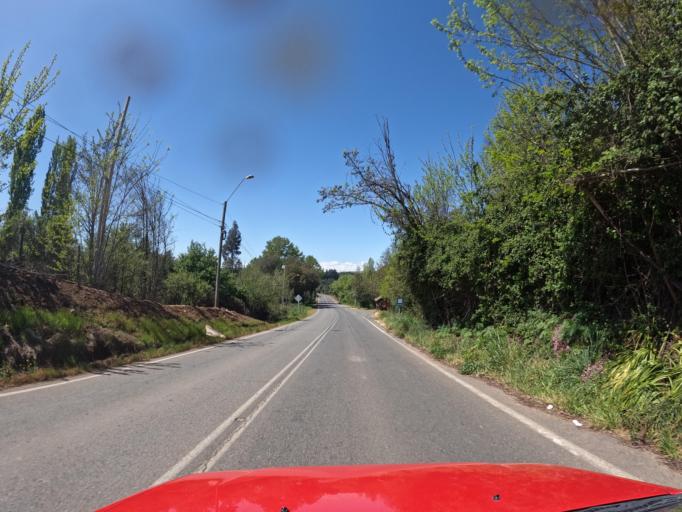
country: CL
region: Maule
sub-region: Provincia de Talca
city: San Clemente
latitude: -35.4897
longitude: -71.2986
